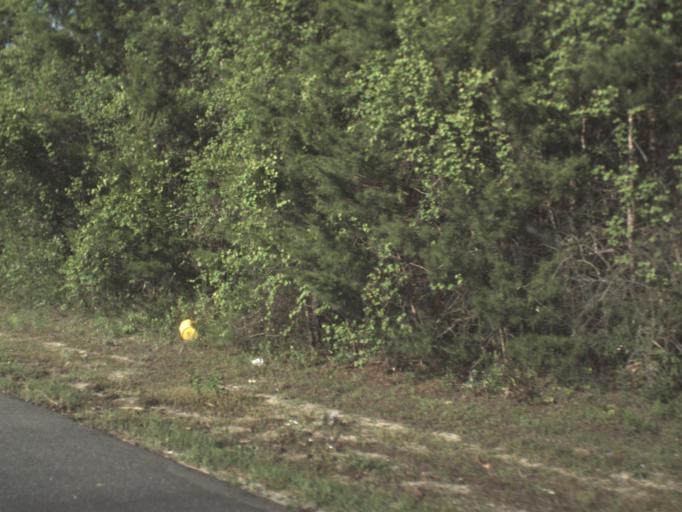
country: US
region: Florida
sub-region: Liberty County
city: Bristol
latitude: 30.4340
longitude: -84.7717
